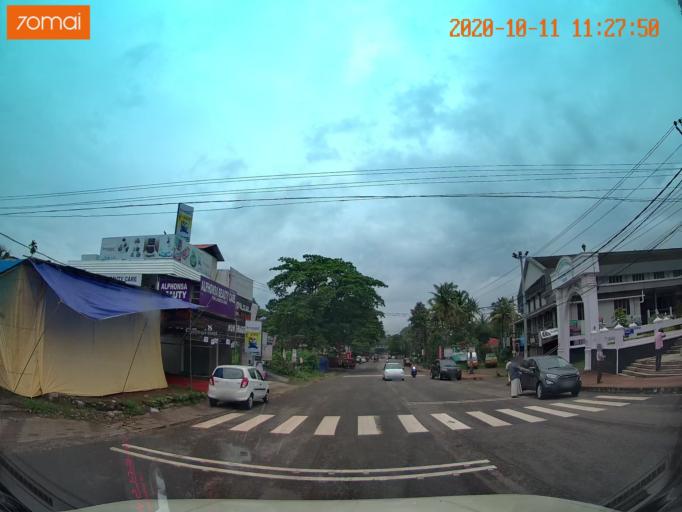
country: IN
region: Kerala
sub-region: Kottayam
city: Changanacheri
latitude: 9.4558
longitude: 76.5511
